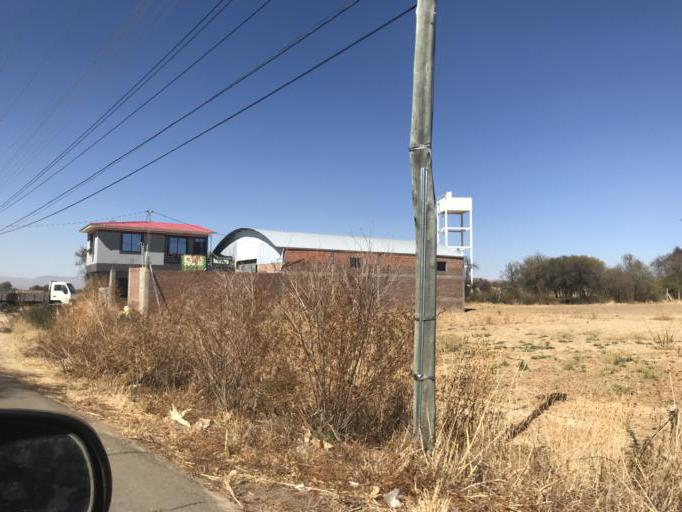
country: BO
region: Cochabamba
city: Tarata
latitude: -17.6089
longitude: -66.0054
